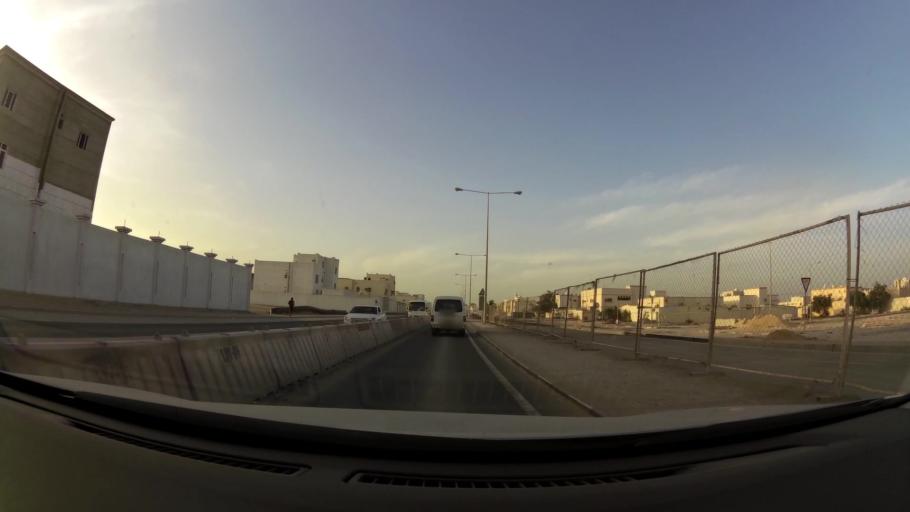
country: QA
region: Al Wakrah
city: Al Wakrah
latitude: 25.1539
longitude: 51.5930
